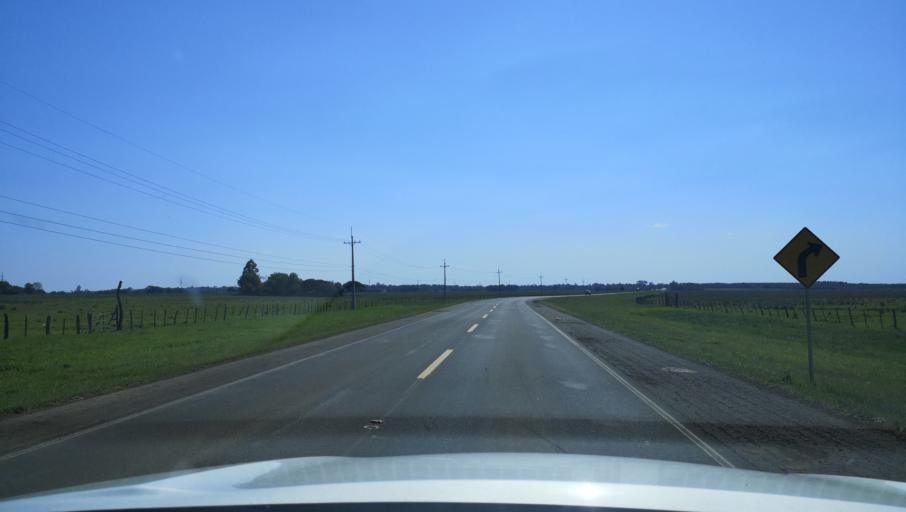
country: PY
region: Itapua
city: General Delgado
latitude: -27.0838
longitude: -56.5553
